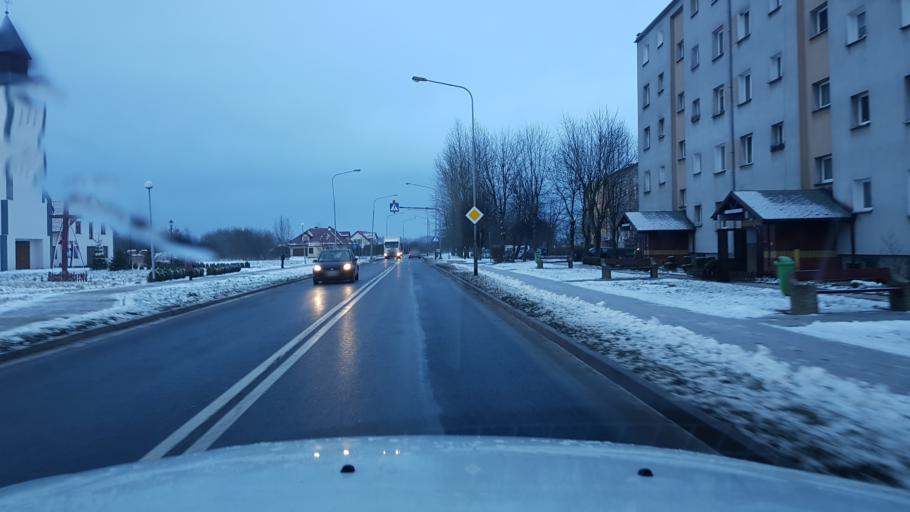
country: PL
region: West Pomeranian Voivodeship
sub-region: Powiat drawski
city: Zlocieniec
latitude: 53.5342
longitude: 16.0216
